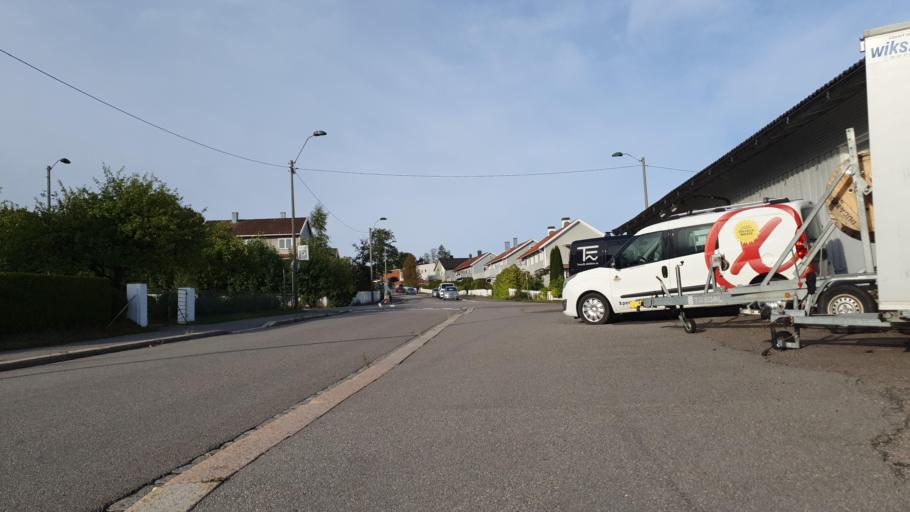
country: NO
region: Vestfold
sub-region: Tonsberg
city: Tonsberg
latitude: 59.2766
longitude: 10.4198
